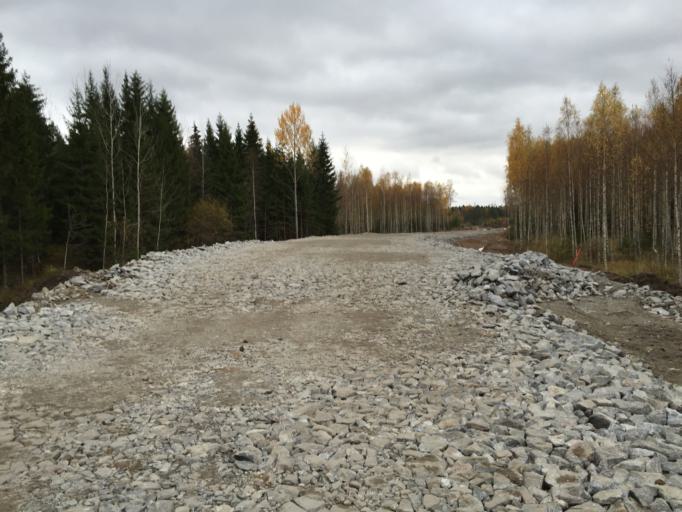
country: SE
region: Vaestmanland
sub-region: Hallstahammars Kommun
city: Hallstahammar
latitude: 59.6386
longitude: 16.2076
